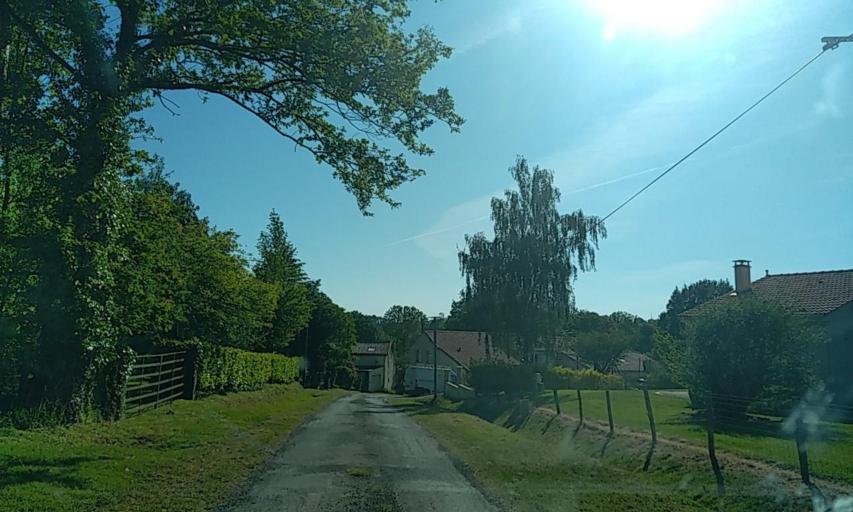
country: FR
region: Poitou-Charentes
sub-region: Departement des Deux-Sevres
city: Boisme
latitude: 46.7956
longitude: -0.4395
